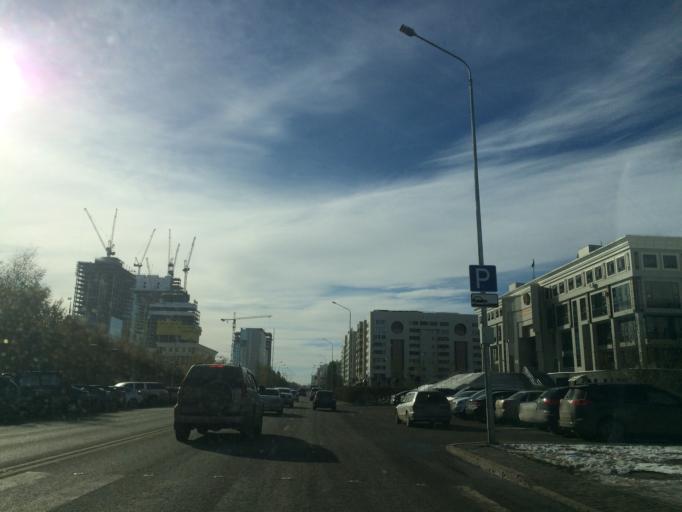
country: KZ
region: Astana Qalasy
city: Astana
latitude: 51.1280
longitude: 71.4283
